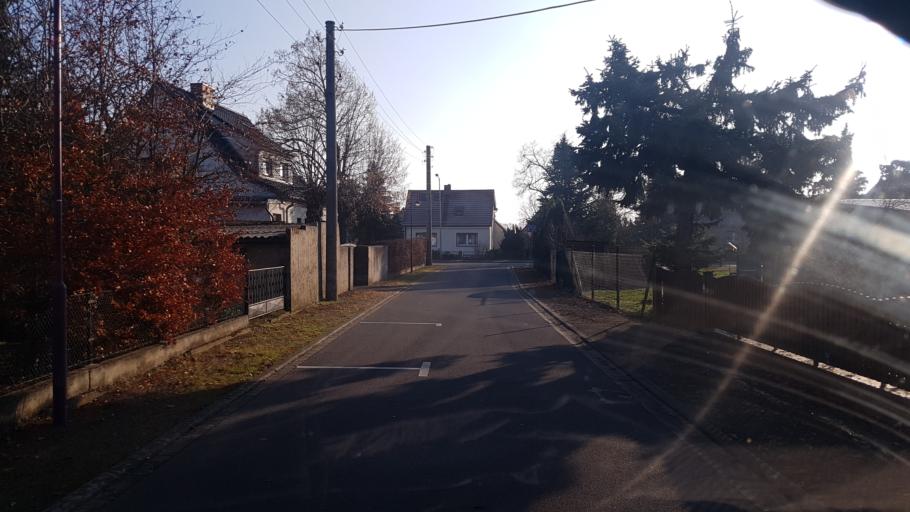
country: DE
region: Brandenburg
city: Lauchhammer
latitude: 51.4716
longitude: 13.7676
